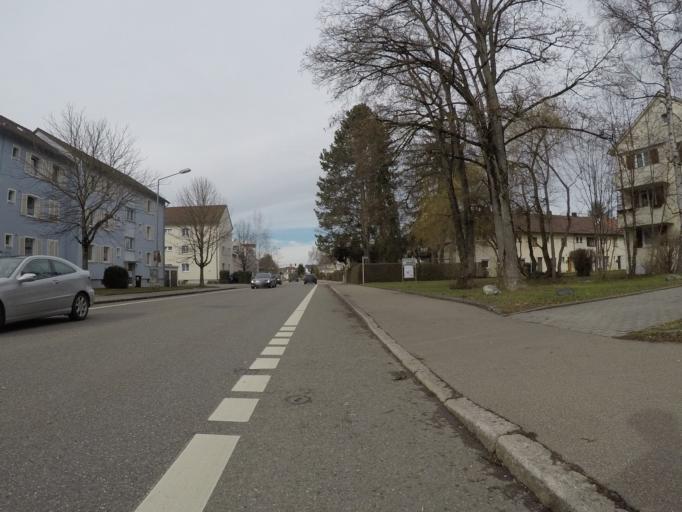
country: DE
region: Baden-Wuerttemberg
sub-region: Tuebingen Region
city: Reutlingen
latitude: 48.4996
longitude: 9.1900
